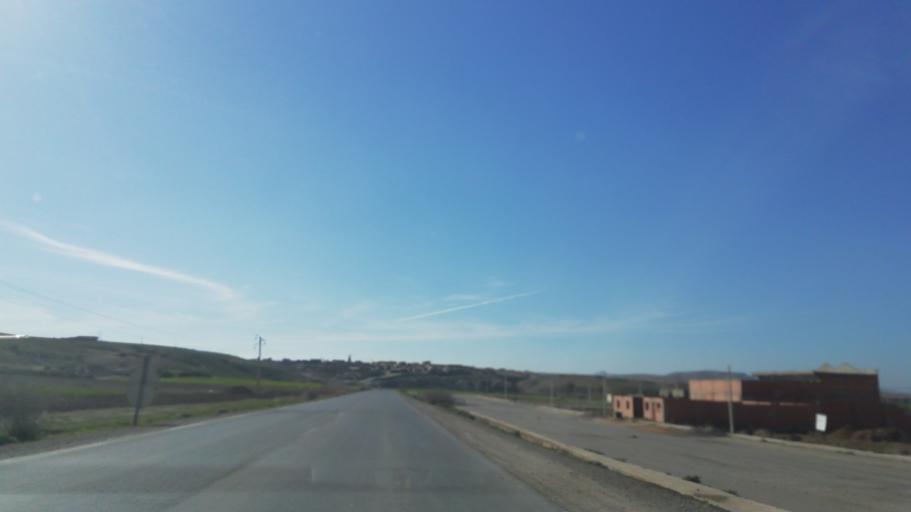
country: DZ
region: Mascara
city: Oued el Abtal
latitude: 35.4555
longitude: 0.7232
